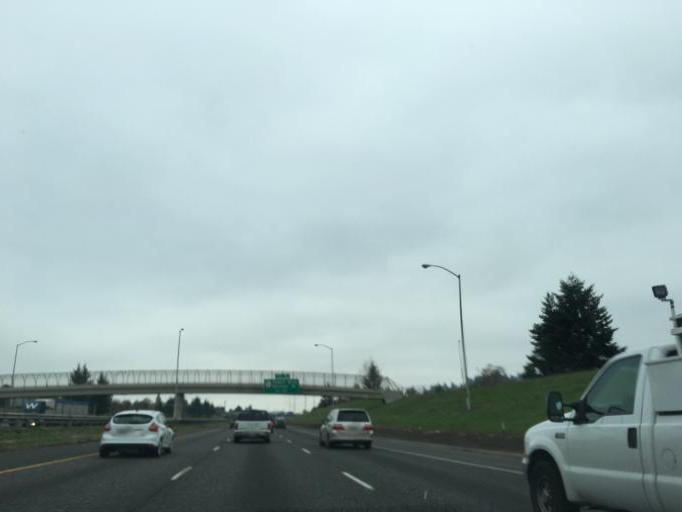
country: US
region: Oregon
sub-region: Multnomah County
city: Lents
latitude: 45.4834
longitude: -122.5658
